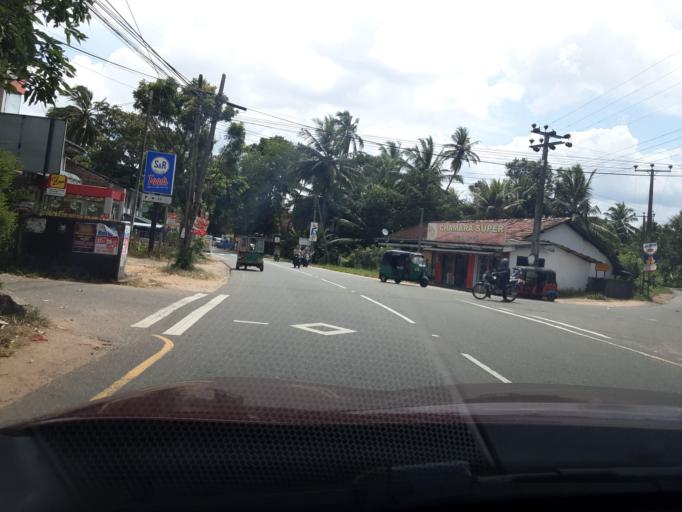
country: LK
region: North Western
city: Kuliyapitiya
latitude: 7.4504
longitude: 80.1854
